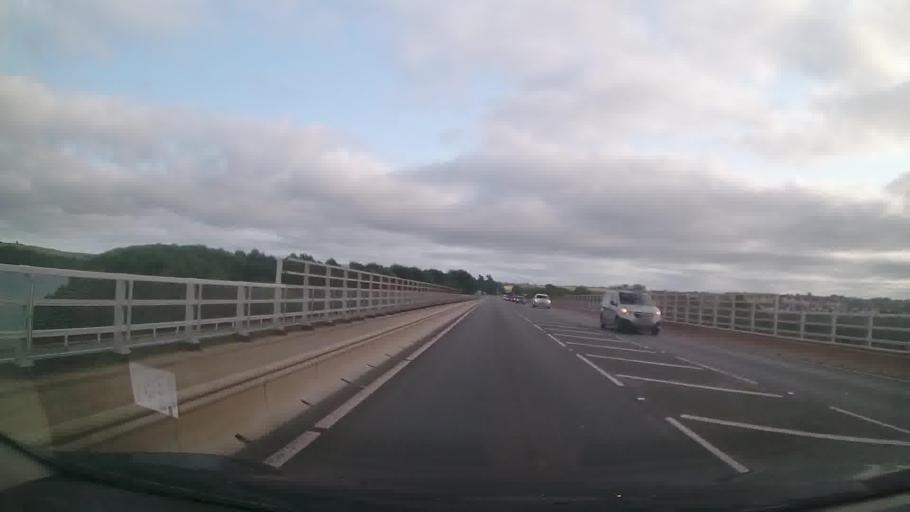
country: GB
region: Wales
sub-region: Pembrokeshire
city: Burton
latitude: 51.7051
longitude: -4.9328
